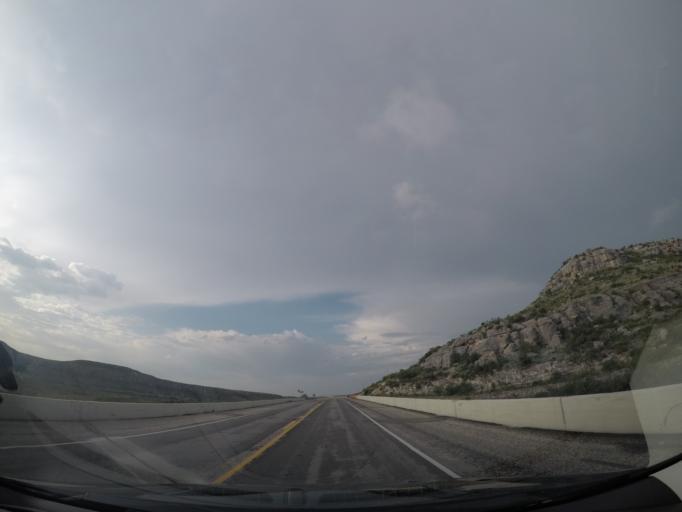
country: US
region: Texas
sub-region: Terrell County
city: Sanderson
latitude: 30.1045
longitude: -102.3641
